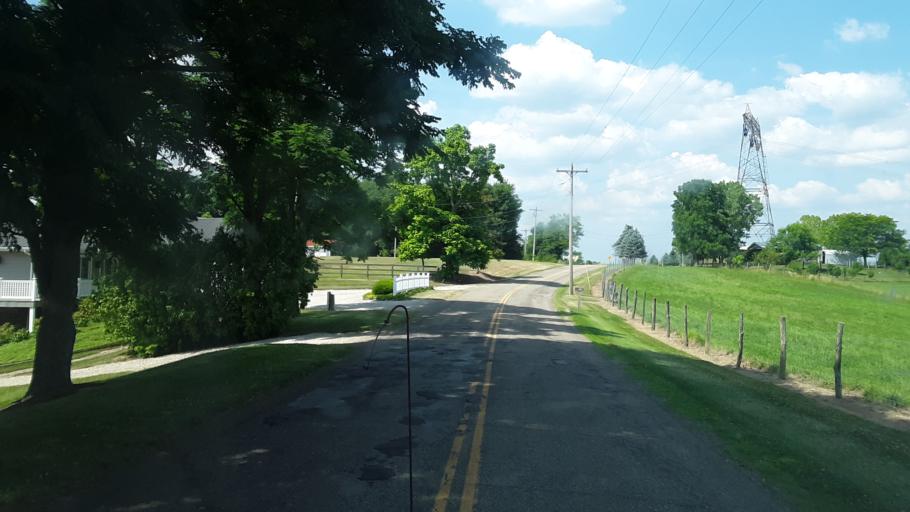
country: US
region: Ohio
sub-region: Carroll County
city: Carrollton
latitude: 40.5372
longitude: -81.0855
